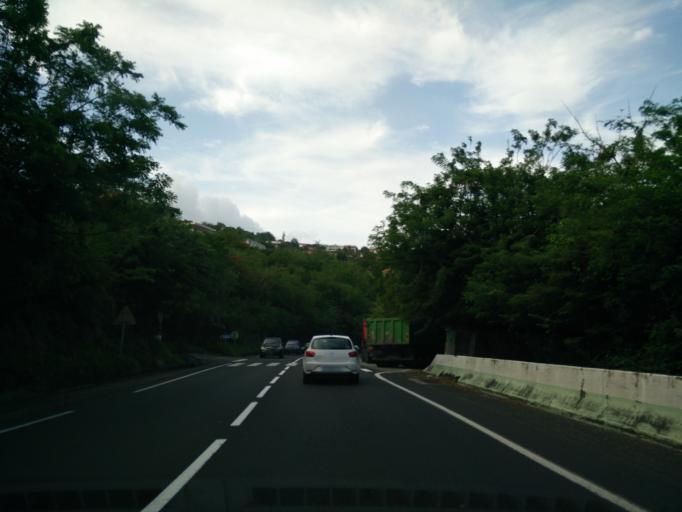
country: MQ
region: Martinique
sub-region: Martinique
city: Fort-de-France
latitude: 14.6332
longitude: -61.1282
